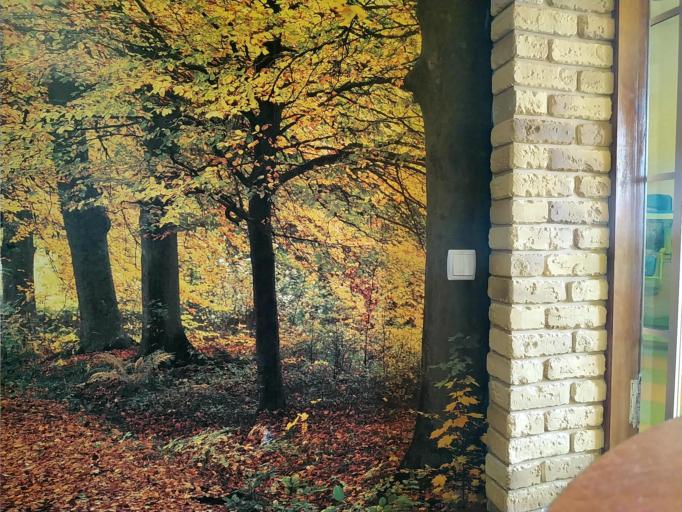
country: RU
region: Smolensk
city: Katyn'
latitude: 54.9341
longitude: 31.7349
